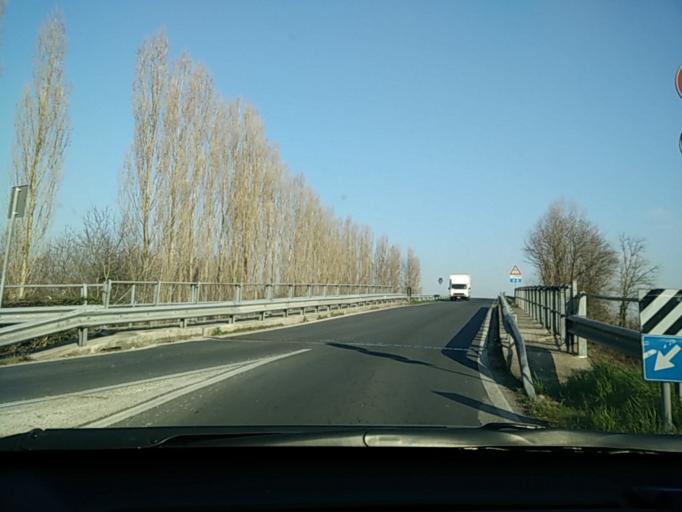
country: IT
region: Veneto
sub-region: Provincia di Treviso
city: San Biagio di Callalta
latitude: 45.6829
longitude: 12.3637
